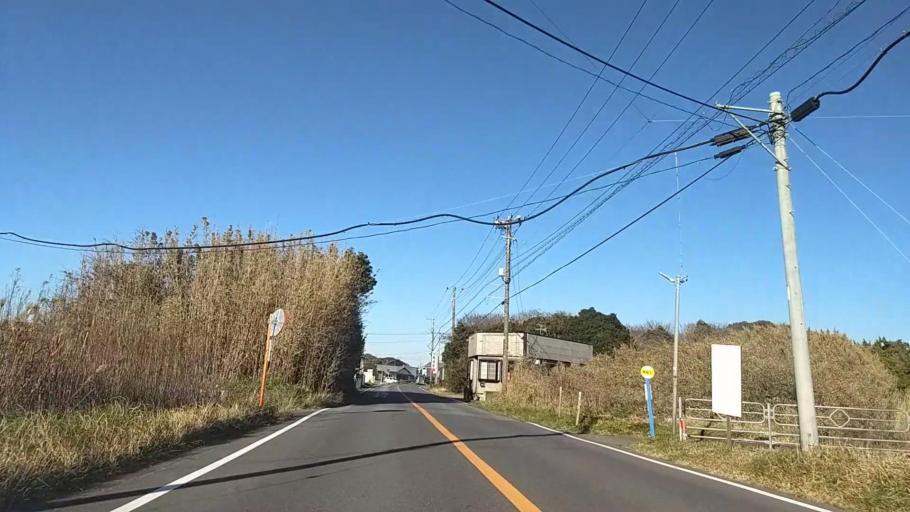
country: JP
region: Chiba
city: Naruto
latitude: 35.6037
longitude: 140.5172
